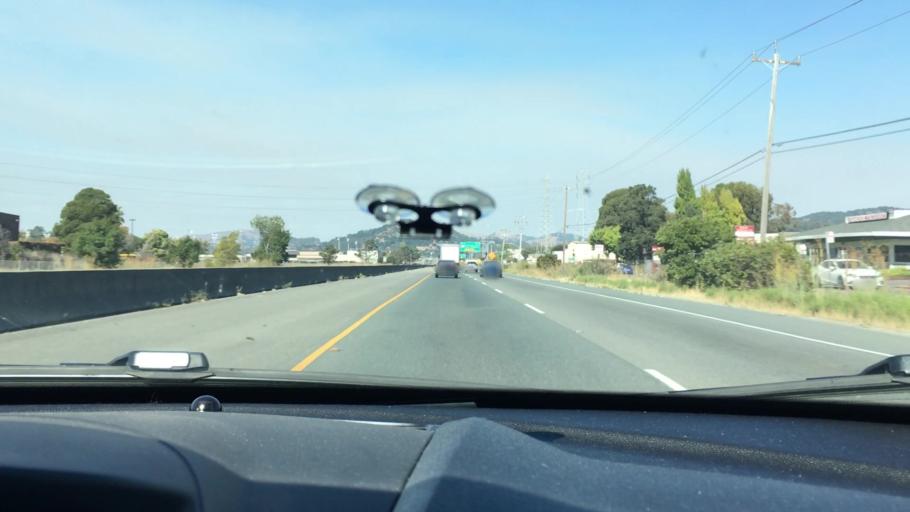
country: US
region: California
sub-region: Marin County
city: San Rafael
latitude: 37.9534
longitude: -122.4984
